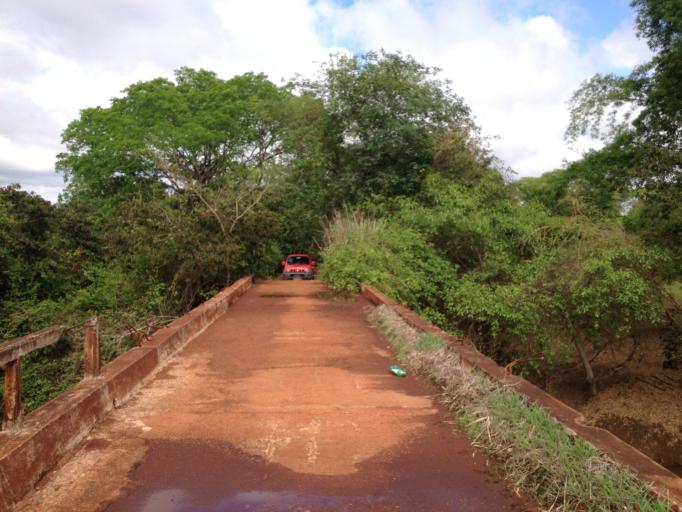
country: BR
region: Minas Gerais
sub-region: Capinopolis
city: Capinopolis
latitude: -18.3492
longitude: -49.6017
